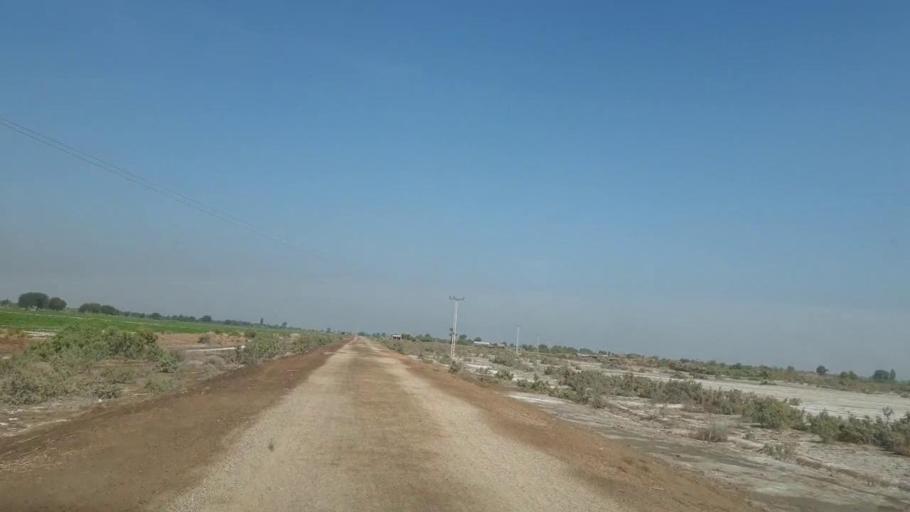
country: PK
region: Sindh
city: Mirpur Khas
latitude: 25.5695
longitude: 69.1849
